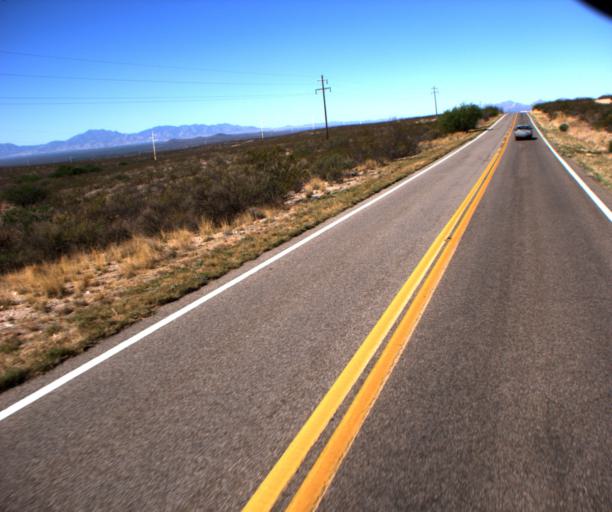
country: US
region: Arizona
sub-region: Cochise County
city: Tombstone
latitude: 31.7442
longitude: -110.1347
